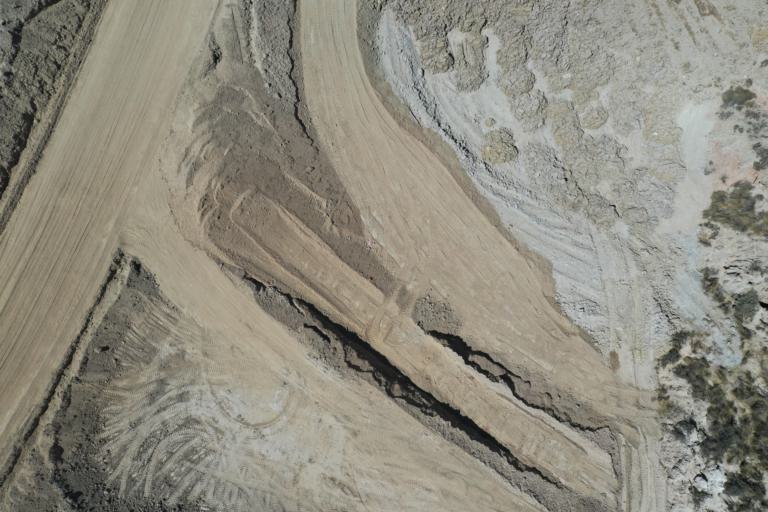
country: BO
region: La Paz
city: La Paz
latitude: -16.5580
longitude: -68.1301
